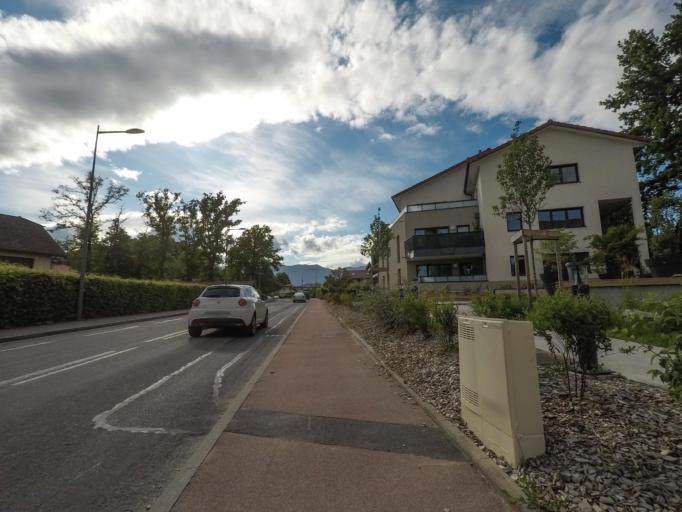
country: CH
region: Geneva
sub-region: Geneva
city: Meyrin
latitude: 46.2555
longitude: 6.0779
